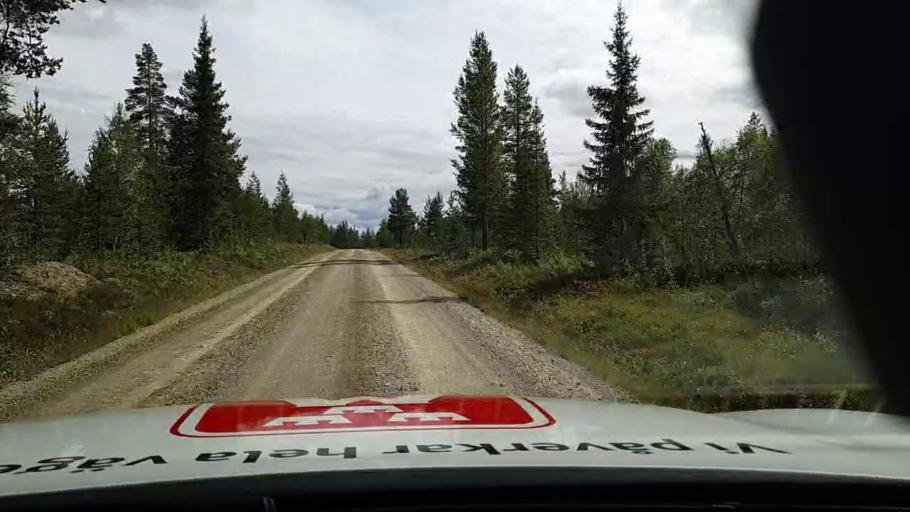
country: SE
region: Jaemtland
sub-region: Are Kommun
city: Jarpen
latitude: 62.5383
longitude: 13.4757
